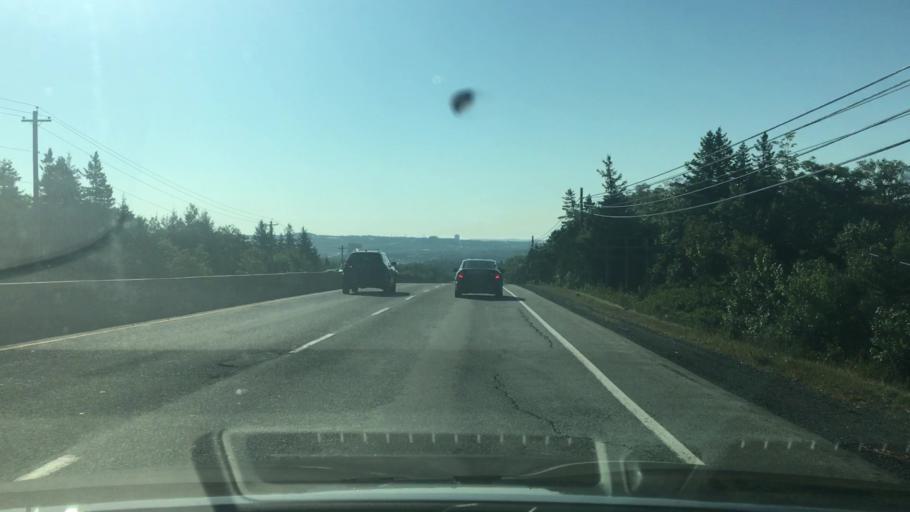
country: CA
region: Nova Scotia
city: Dartmouth
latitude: 44.7165
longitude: -63.6334
